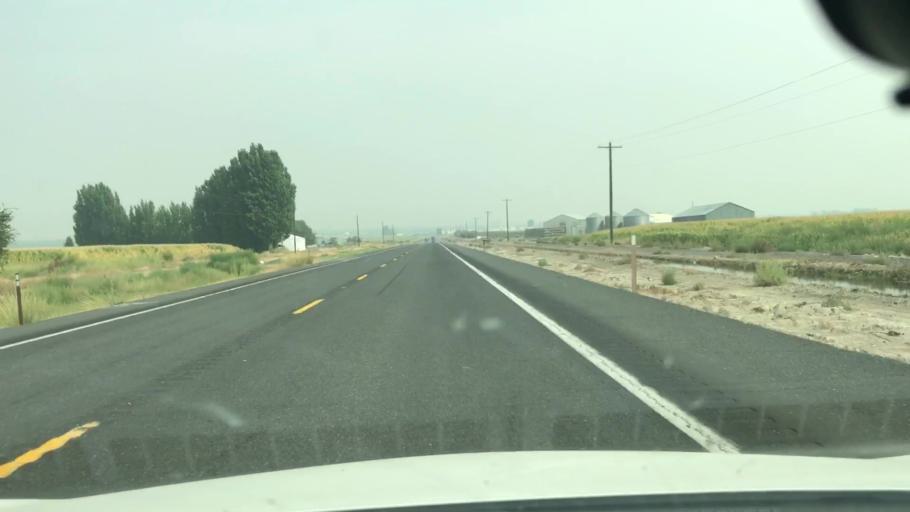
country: US
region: Washington
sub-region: Grant County
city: Quincy
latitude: 47.2392
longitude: -119.7397
